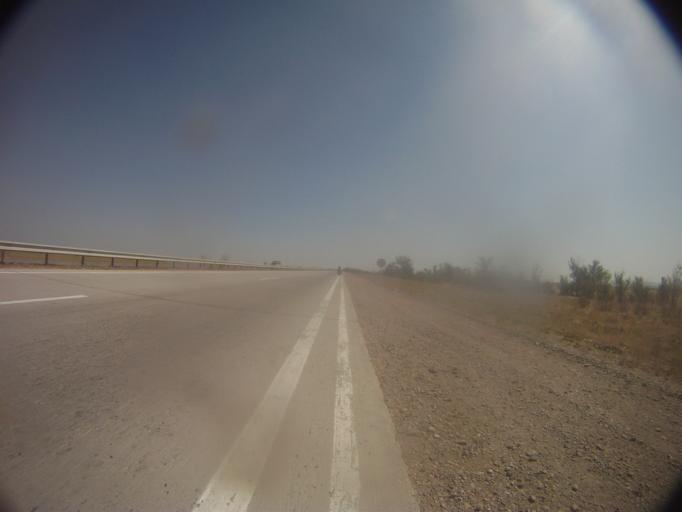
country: KZ
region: Zhambyl
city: Taraz
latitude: 42.7986
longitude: 71.0913
